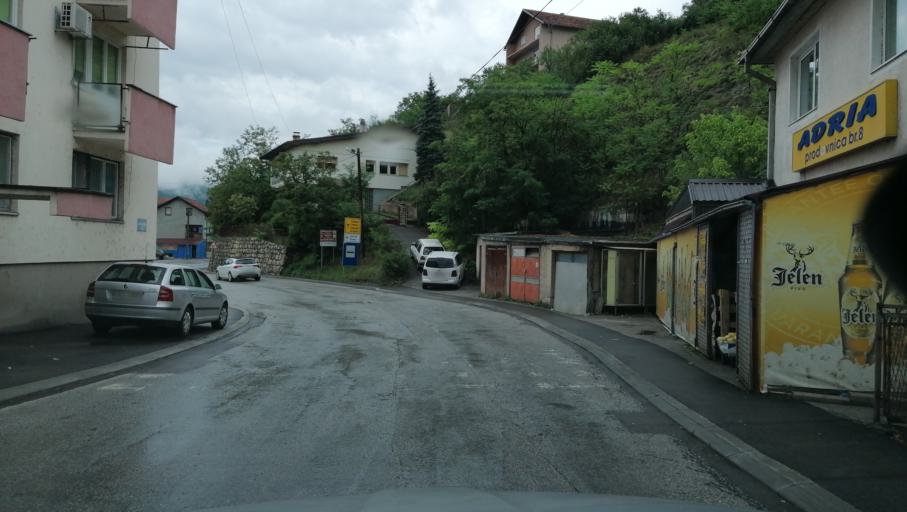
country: BA
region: Republika Srpska
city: Visegrad
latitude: 43.7856
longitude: 19.2963
